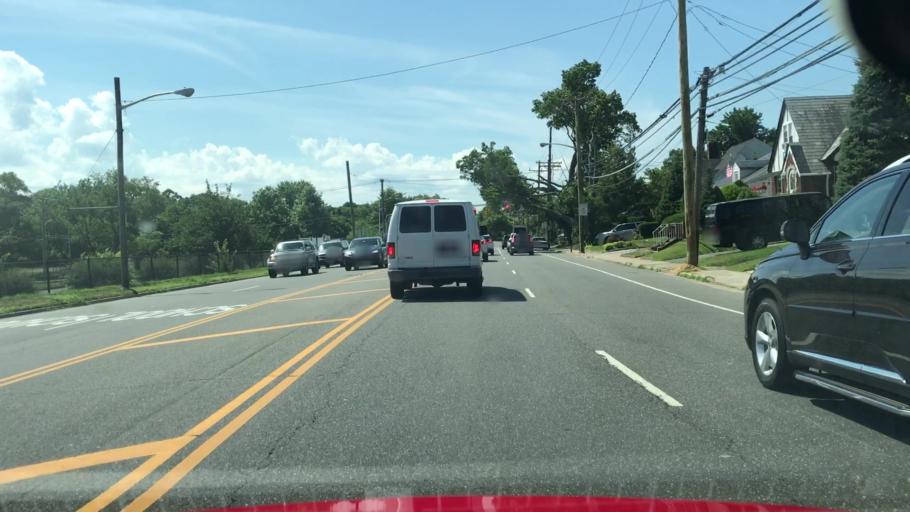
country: US
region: New York
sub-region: Nassau County
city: Malverne
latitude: 40.6684
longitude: -73.6610
